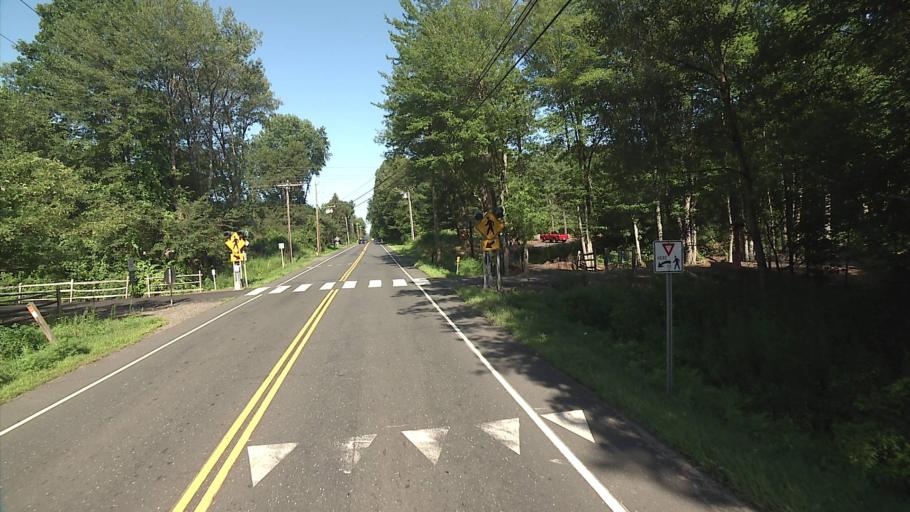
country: US
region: Connecticut
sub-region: Hartford County
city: Salmon Brook
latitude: 41.9532
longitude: -72.7683
